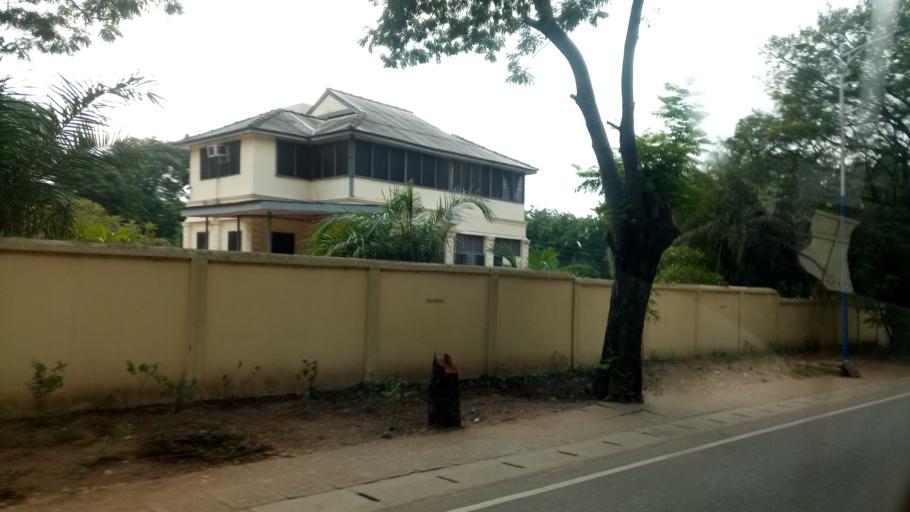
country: GH
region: Greater Accra
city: Accra
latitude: 5.5570
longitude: -0.1947
